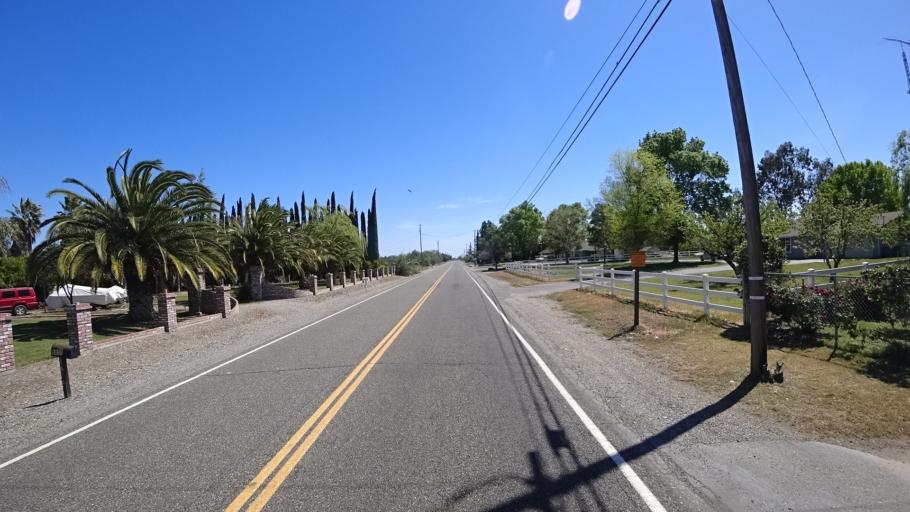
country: US
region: California
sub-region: Glenn County
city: Orland
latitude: 39.7313
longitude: -122.1562
